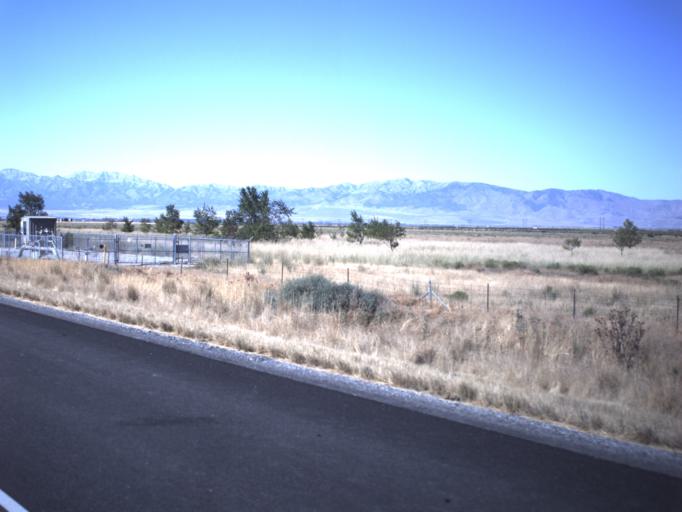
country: US
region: Utah
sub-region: Tooele County
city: Stansbury park
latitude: 40.6695
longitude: -112.2829
